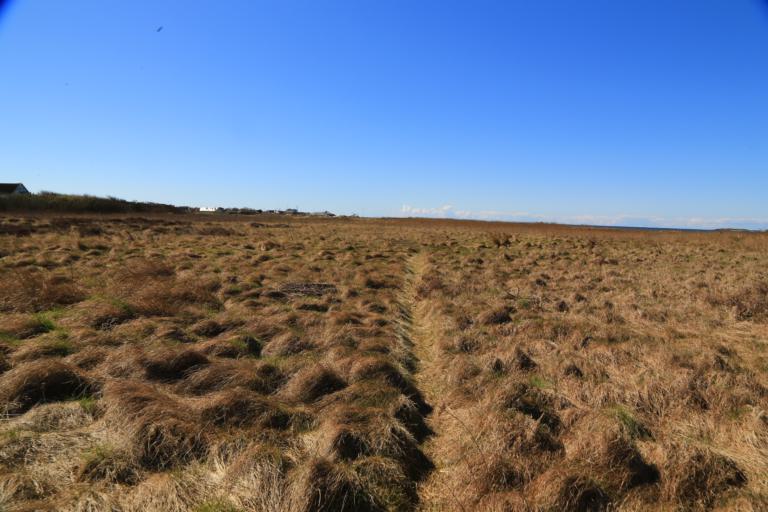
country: SE
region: Halland
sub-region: Varbergs Kommun
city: Traslovslage
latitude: 57.0648
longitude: 12.2788
